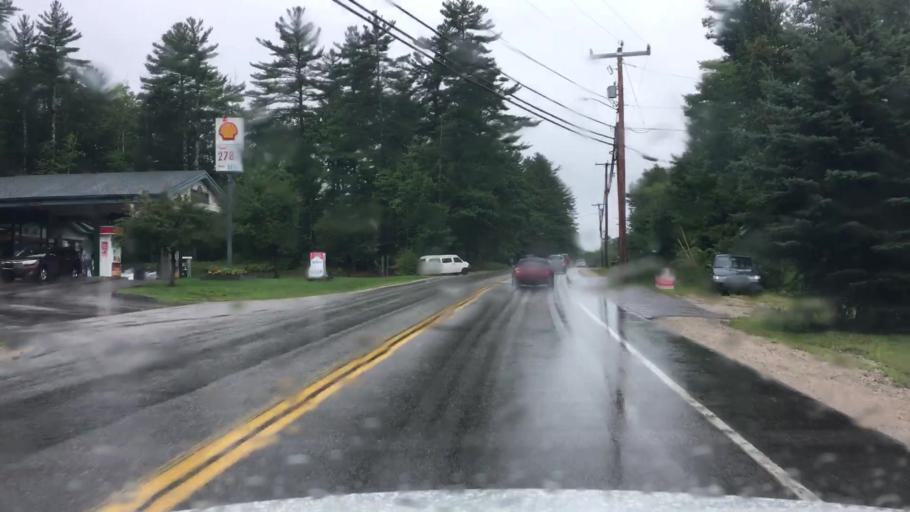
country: US
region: New Hampshire
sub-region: Carroll County
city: Conway
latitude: 43.9957
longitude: -71.0654
